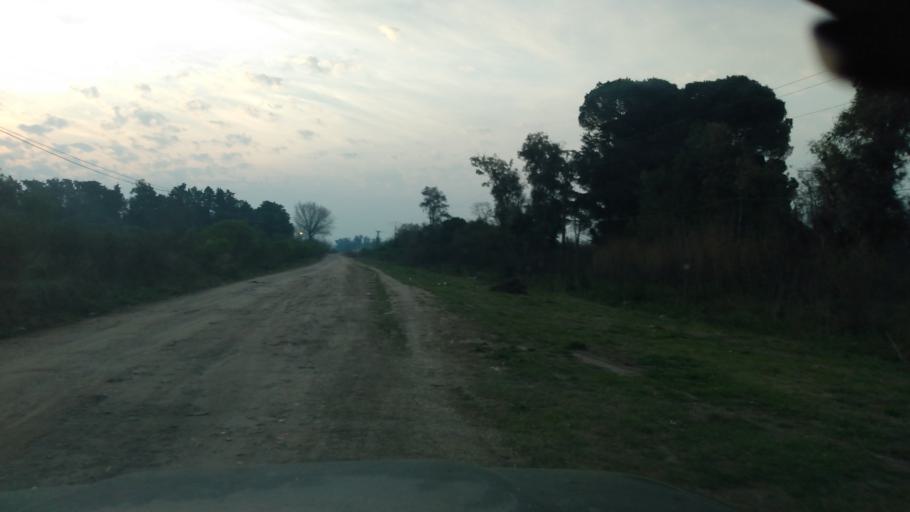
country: AR
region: Buenos Aires
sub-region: Partido de Lujan
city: Lujan
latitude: -34.5587
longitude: -59.1348
